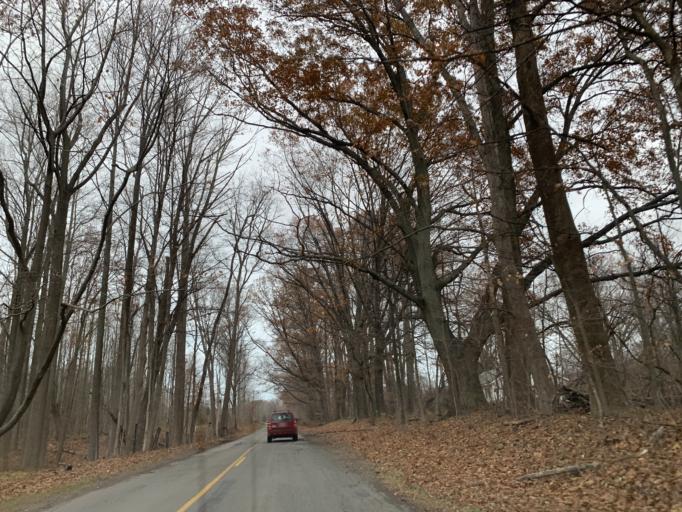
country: US
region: Michigan
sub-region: Berrien County
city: Three Oaks
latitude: 41.8172
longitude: -86.6683
